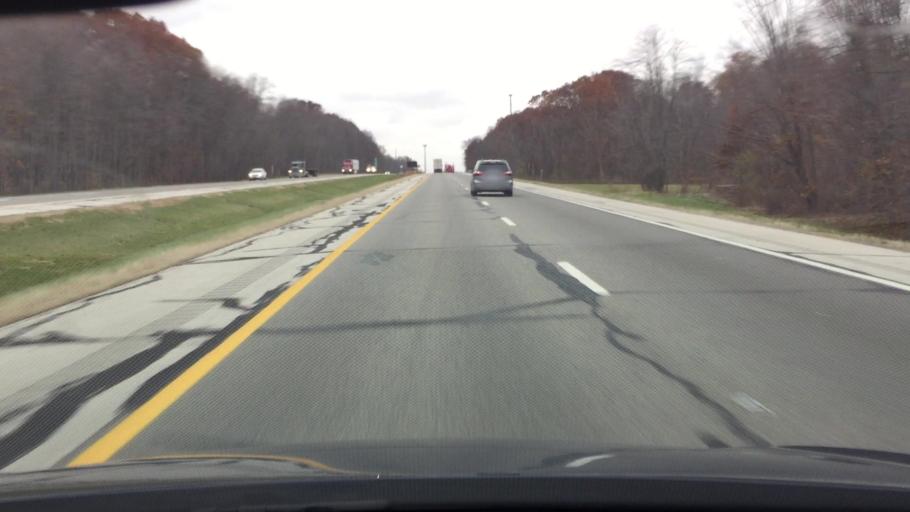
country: US
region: Ohio
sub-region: Mahoning County
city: Canfield
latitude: 41.0357
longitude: -80.7466
